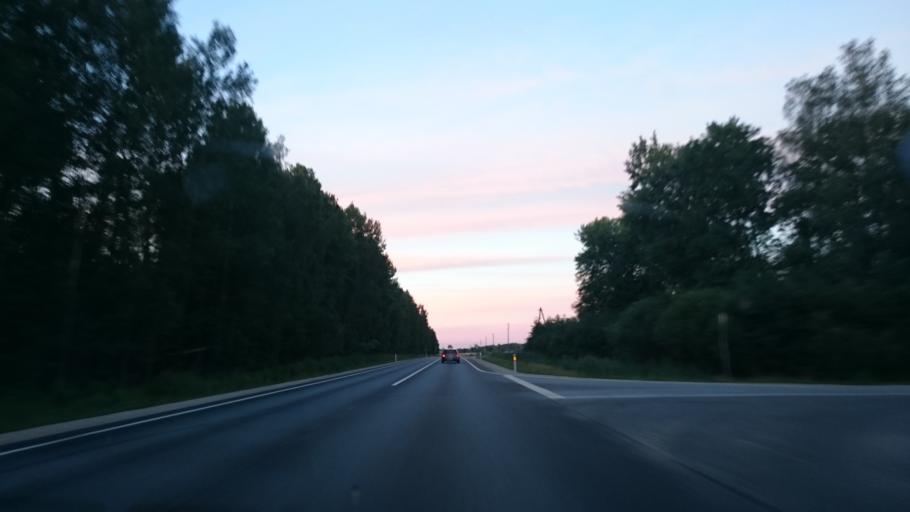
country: LV
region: Dobeles Rajons
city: Dobele
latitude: 56.7582
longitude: 23.2908
